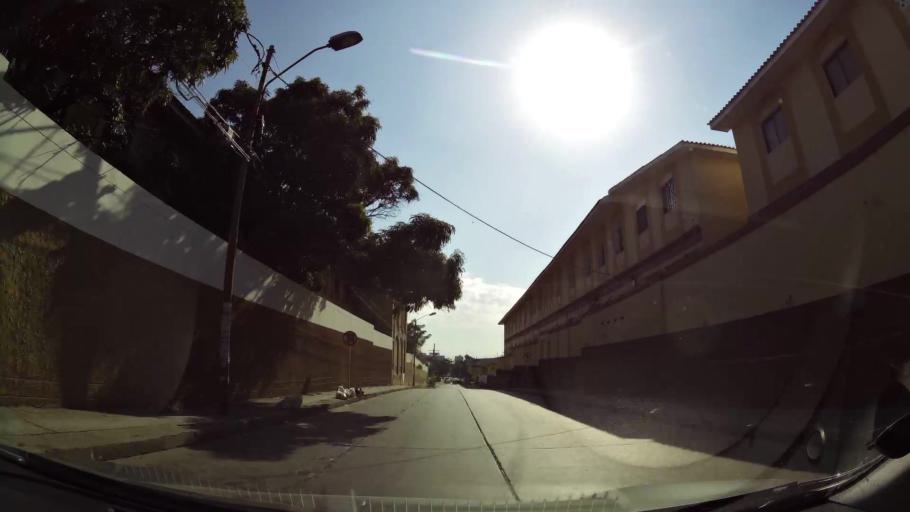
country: CO
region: Atlantico
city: Barranquilla
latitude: 10.9818
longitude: -74.7888
